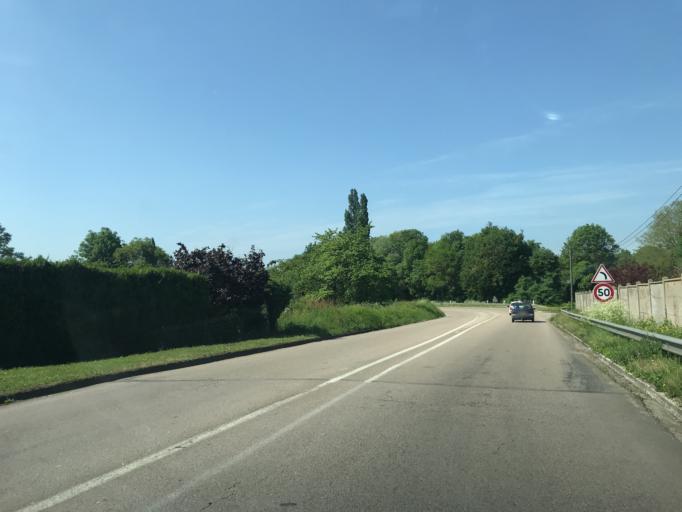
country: FR
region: Haute-Normandie
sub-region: Departement de la Seine-Maritime
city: Les Authieux-sur-le-Port-Saint-Ouen
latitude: 49.3522
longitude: 1.1295
